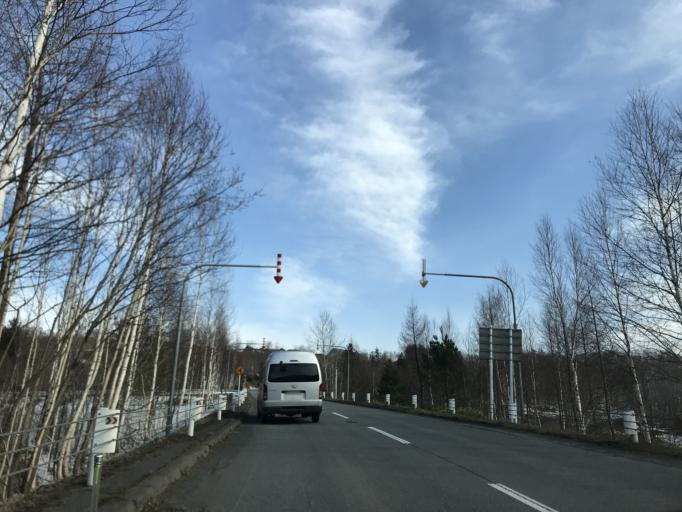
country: JP
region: Hokkaido
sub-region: Asahikawa-shi
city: Asahikawa
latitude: 43.7187
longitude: 142.3189
